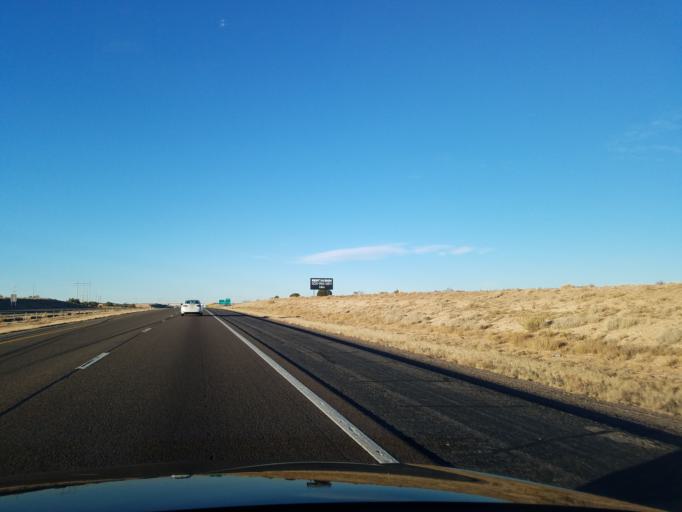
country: US
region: New Mexico
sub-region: Sandoval County
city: Santo Domingo Pueblo
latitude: 35.4741
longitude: -106.2955
